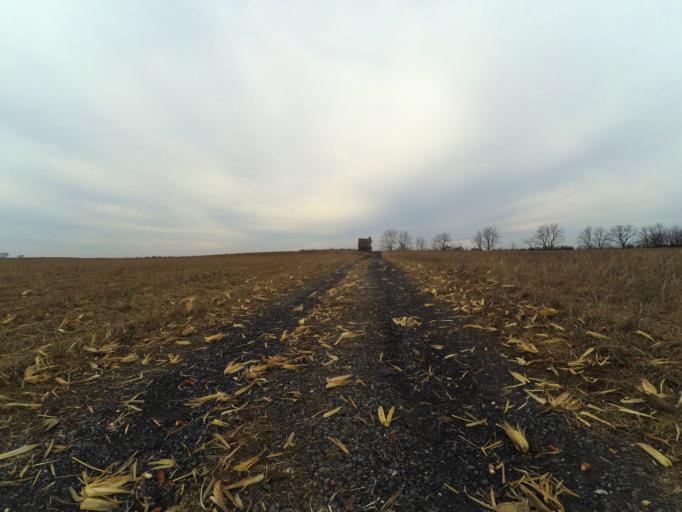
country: US
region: Pennsylvania
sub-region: Centre County
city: State College
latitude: 40.7621
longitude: -77.8540
